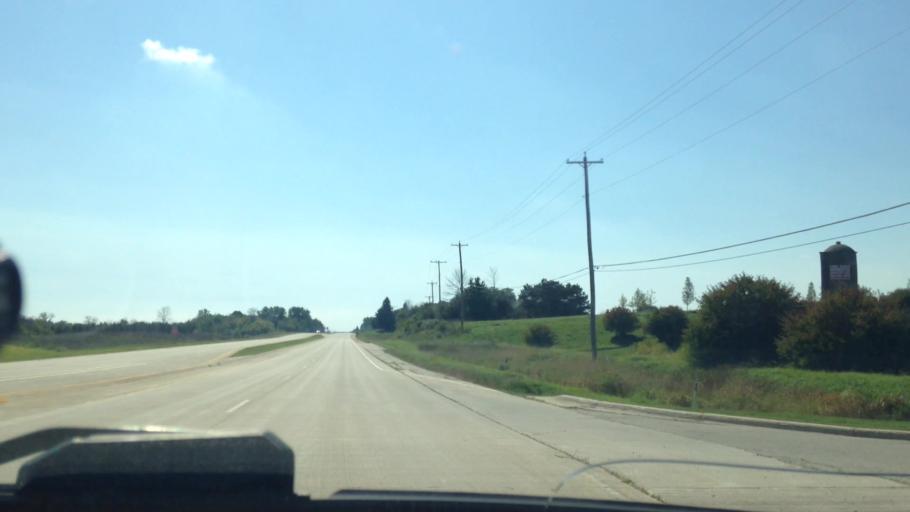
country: US
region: Wisconsin
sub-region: Ozaukee County
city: Port Washington
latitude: 43.3627
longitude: -87.9058
